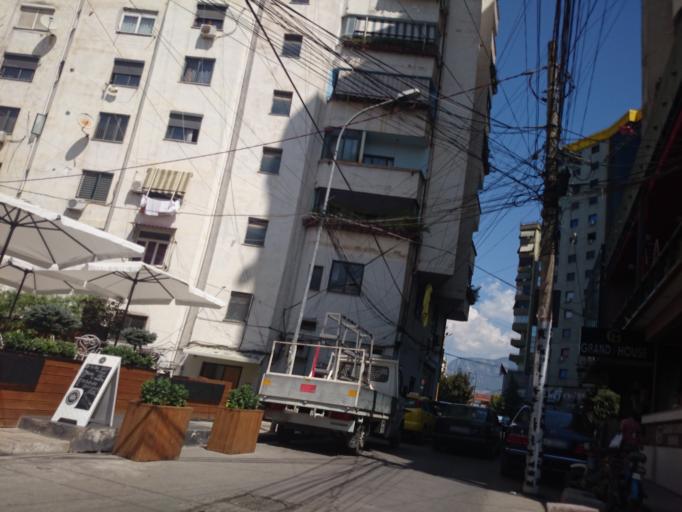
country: AL
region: Tirane
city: Tirana
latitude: 41.3354
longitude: 19.8156
